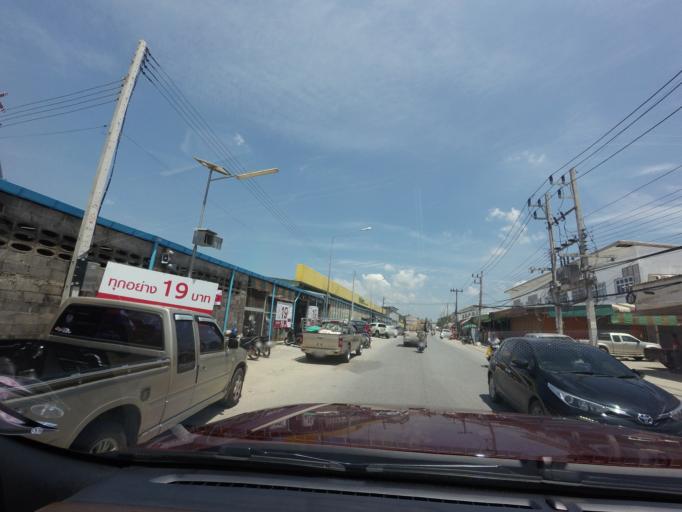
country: TH
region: Yala
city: Yala
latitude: 6.5576
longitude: 101.2746
